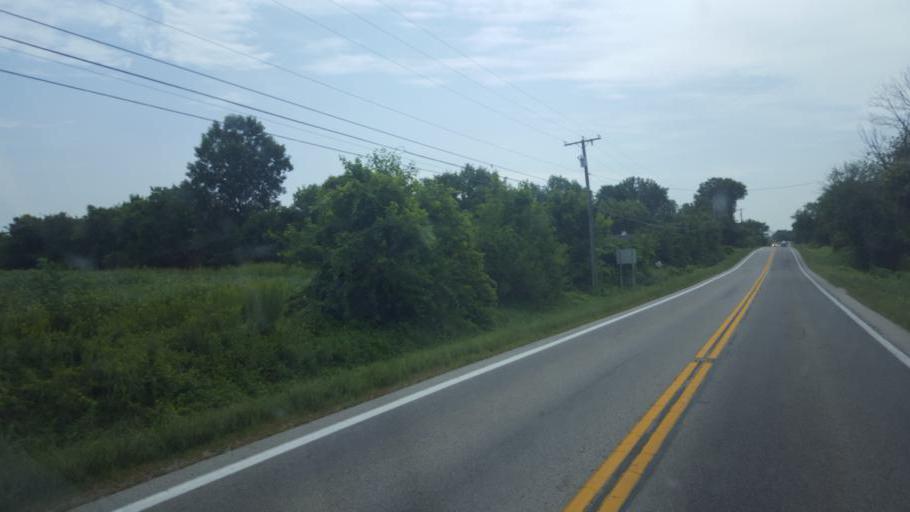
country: US
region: Ohio
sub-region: Marion County
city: Marion
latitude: 40.5172
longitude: -83.0993
